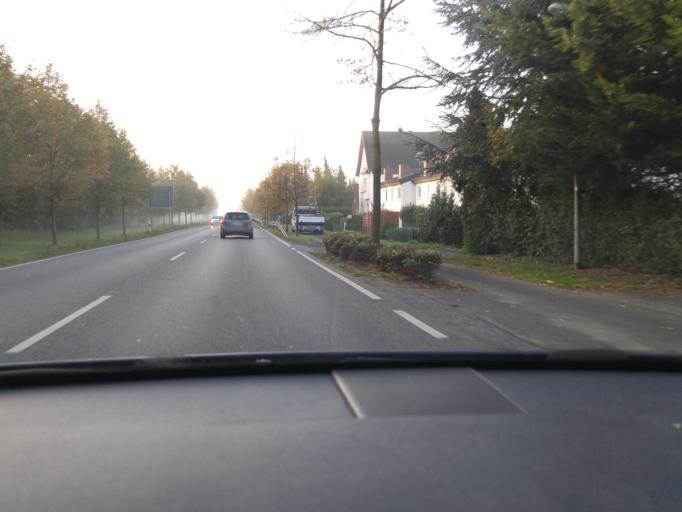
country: DE
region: Hesse
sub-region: Regierungsbezirk Darmstadt
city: Bad Nauheim
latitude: 50.3610
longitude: 8.7510
